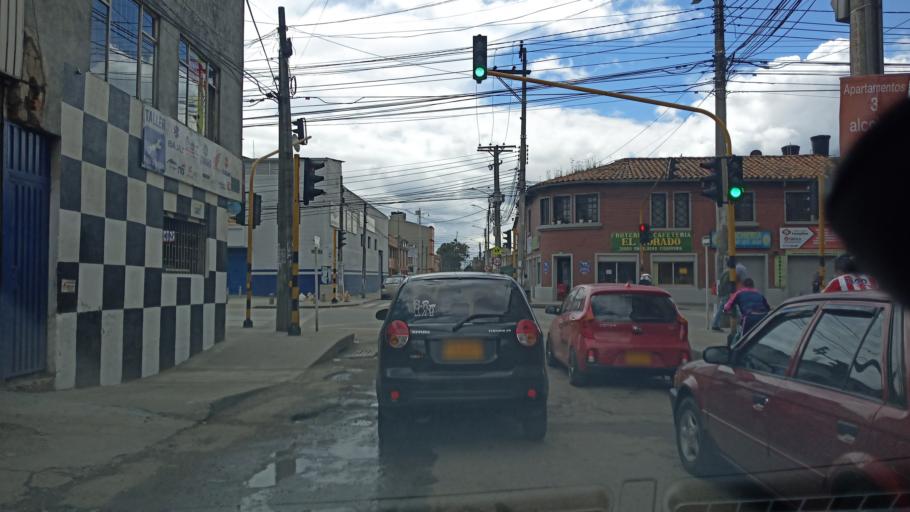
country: CO
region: Cundinamarca
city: Funza
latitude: 4.6710
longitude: -74.1438
